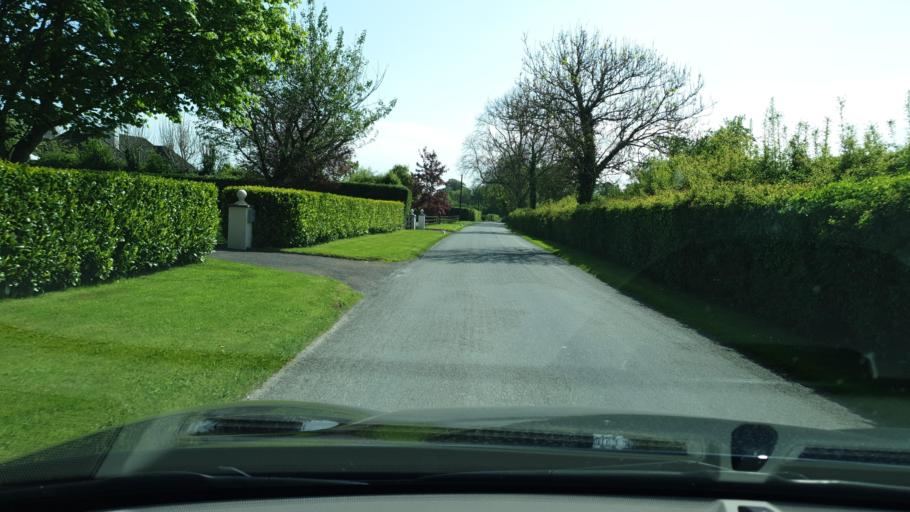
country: IE
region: Leinster
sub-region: An Mhi
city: Dunshaughlin
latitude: 53.4882
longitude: -6.5351
